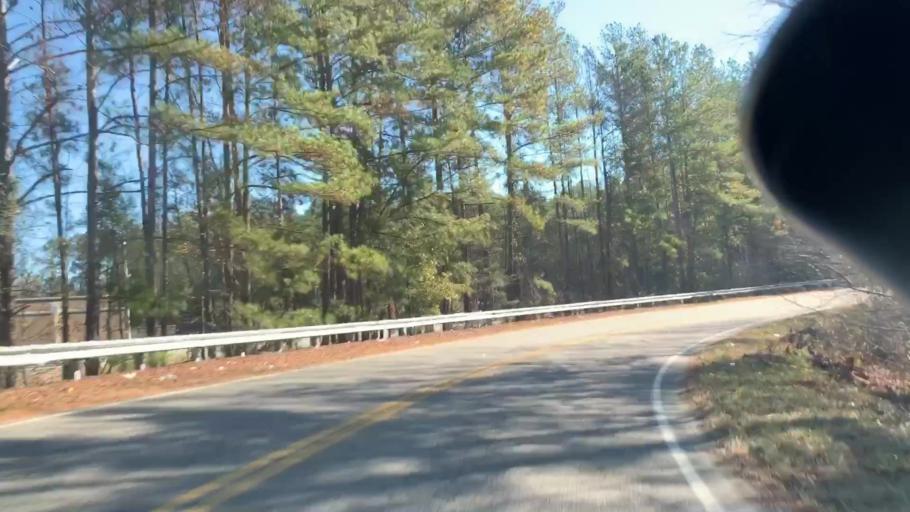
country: US
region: South Carolina
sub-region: Richland County
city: Woodfield
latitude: 34.0732
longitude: -80.9259
